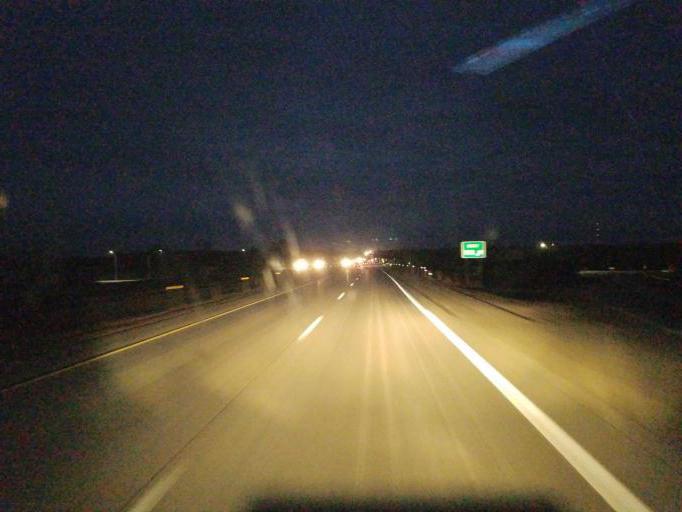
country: US
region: Iowa
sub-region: Guthrie County
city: Guthrie Center
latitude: 41.4961
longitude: -94.5234
